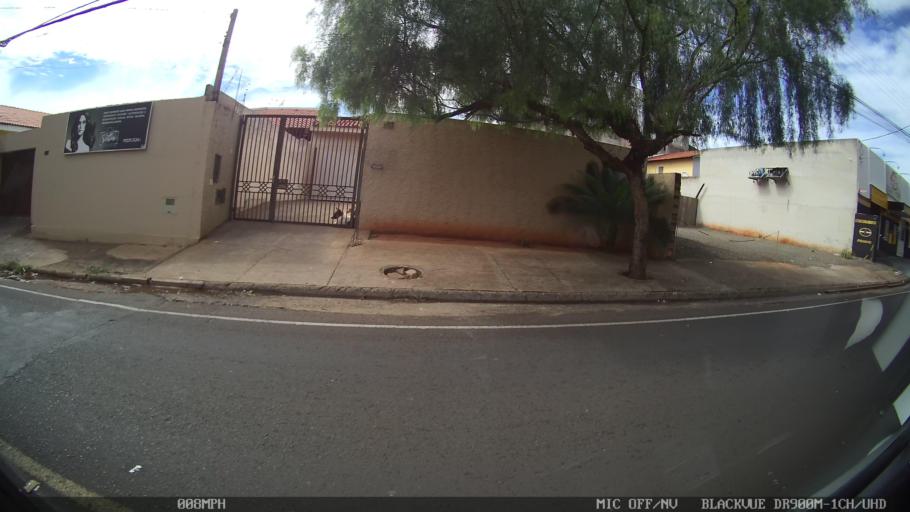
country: BR
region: Sao Paulo
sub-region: Catanduva
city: Catanduva
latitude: -21.1516
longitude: -48.9637
